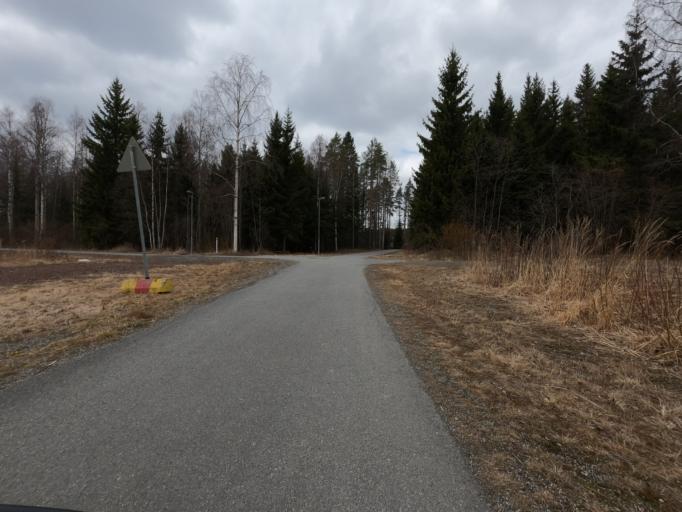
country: FI
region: North Karelia
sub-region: Joensuu
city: Joensuu
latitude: 62.5691
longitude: 29.8139
